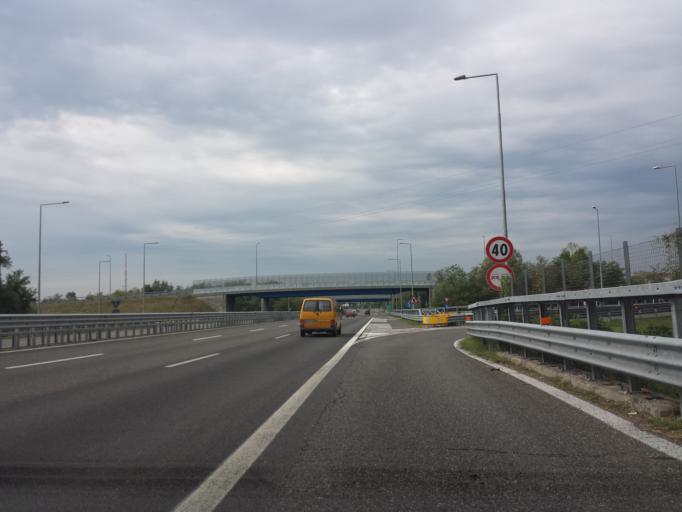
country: IT
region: Lombardy
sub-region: Citta metropolitana di Milano
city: Santa Corinna
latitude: 45.3411
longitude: 9.0996
